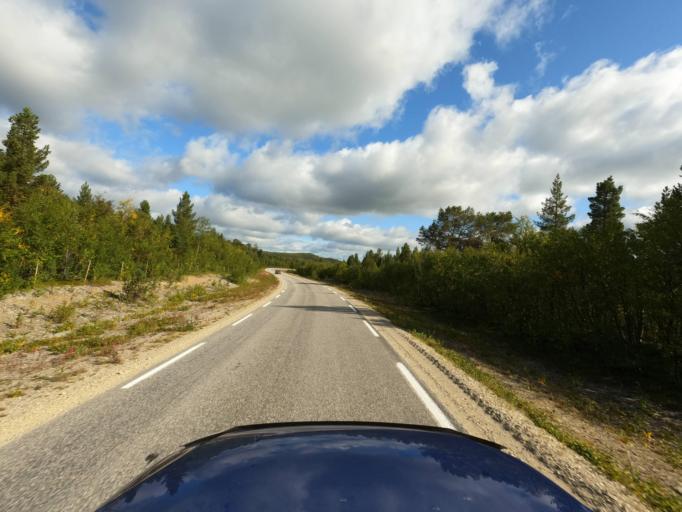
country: NO
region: Finnmark Fylke
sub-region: Karasjok
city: Karasjohka
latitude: 69.4291
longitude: 24.9536
